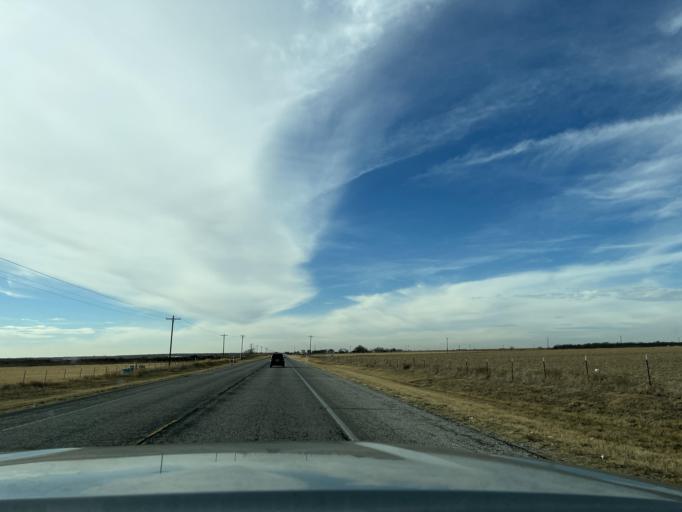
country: US
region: Texas
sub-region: Fisher County
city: Roby
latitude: 32.7557
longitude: -100.2710
